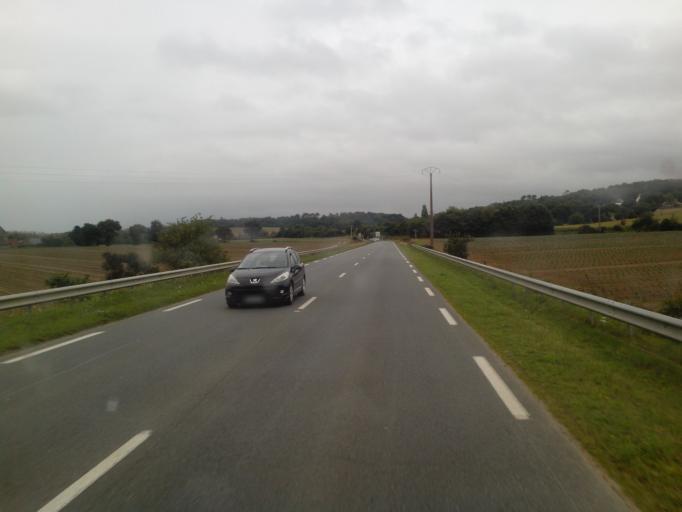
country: FR
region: Brittany
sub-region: Departement des Cotes-d'Armor
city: Plourivo
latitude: 48.7658
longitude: -3.0826
